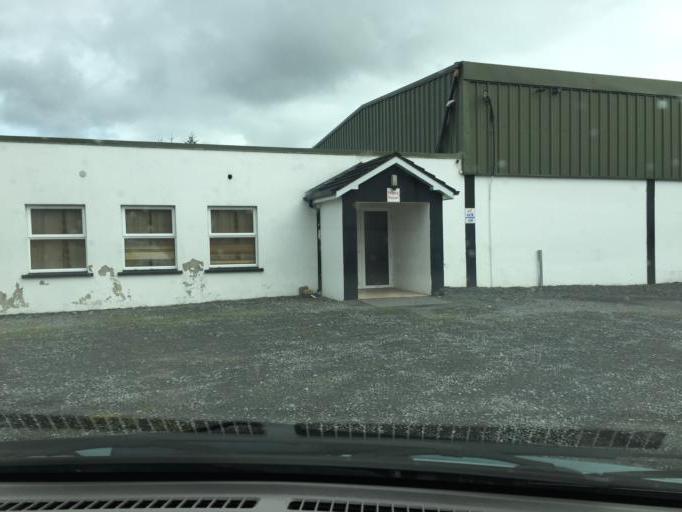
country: IE
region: Connaught
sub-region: Sligo
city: Tobercurry
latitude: 54.0394
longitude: -8.8157
